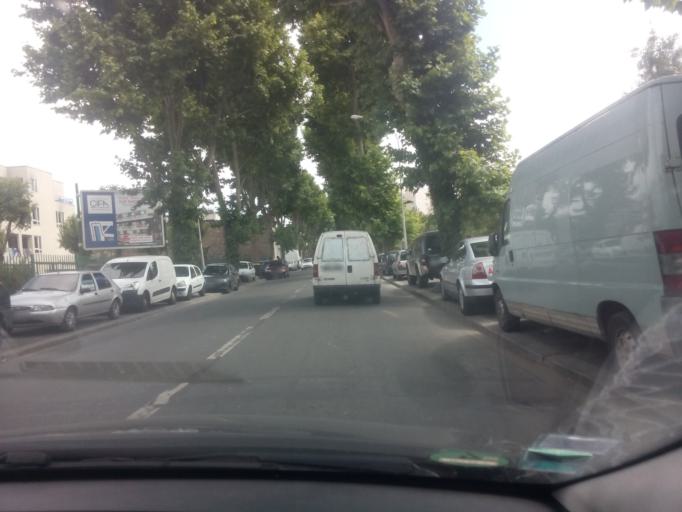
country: FR
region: Ile-de-France
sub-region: Departement de Seine-Saint-Denis
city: Aubervilliers
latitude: 48.9105
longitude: 2.3759
